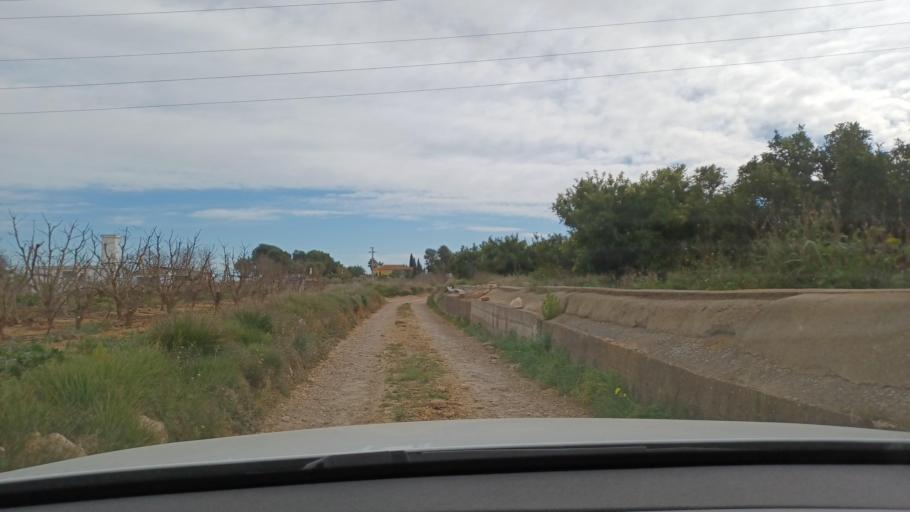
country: ES
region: Valencia
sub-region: Provincia de Valencia
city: Benifaio
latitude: 39.2928
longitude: -0.4456
